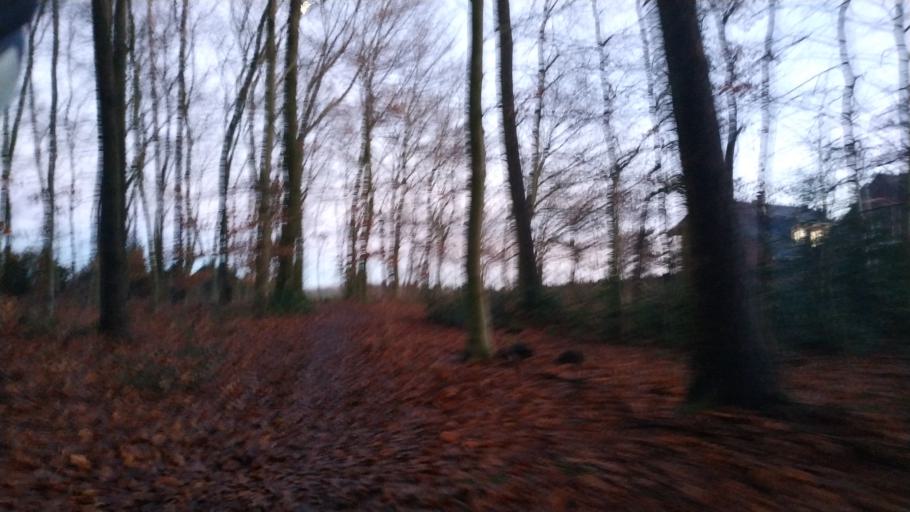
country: DE
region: North Rhine-Westphalia
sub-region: Regierungsbezirk Munster
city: Mettingen
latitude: 52.3160
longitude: 7.7522
